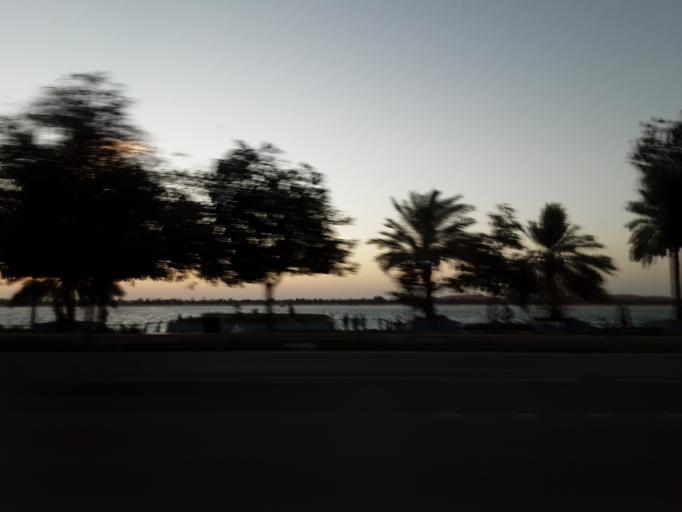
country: AE
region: Abu Dhabi
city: Abu Dhabi
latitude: 24.4927
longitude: 54.3545
